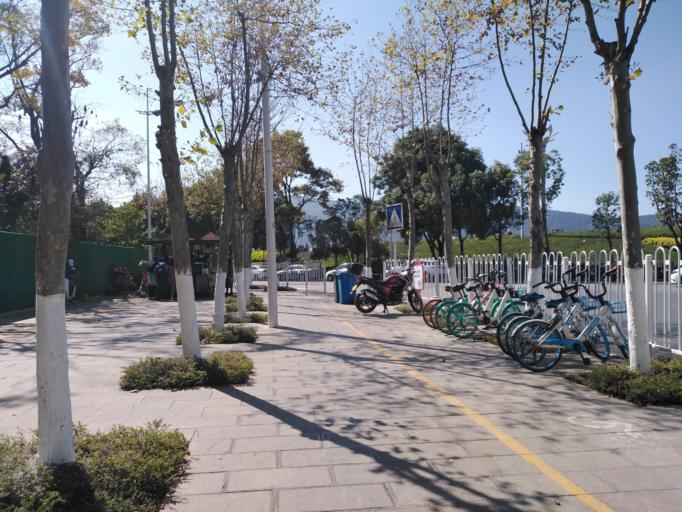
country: CN
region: Yunnan
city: Gaoyao
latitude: 24.9864
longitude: 102.6496
